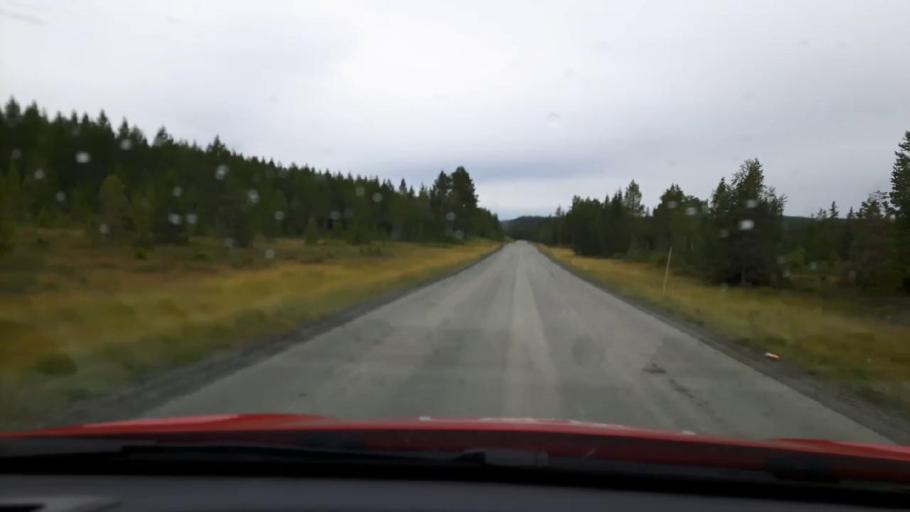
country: SE
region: Jaemtland
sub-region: Are Kommun
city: Are
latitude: 63.4373
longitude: 13.2622
